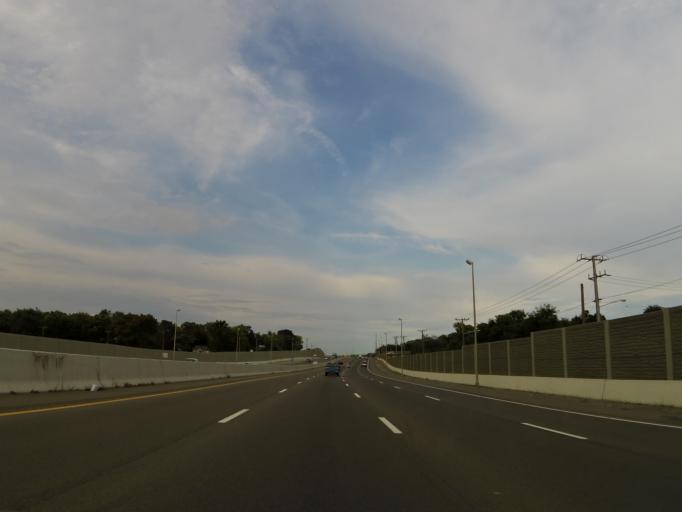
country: US
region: Tennessee
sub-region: Davidson County
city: Belle Meade
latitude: 36.1498
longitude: -86.8716
